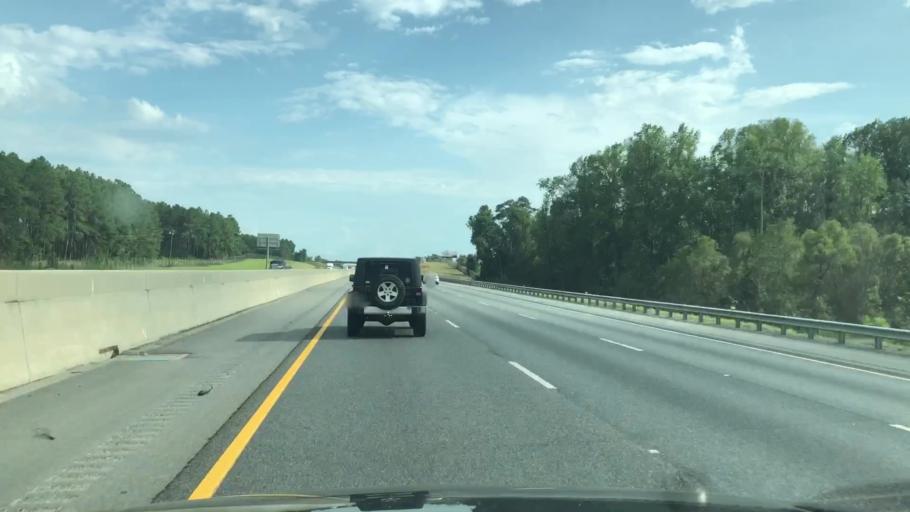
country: US
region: Georgia
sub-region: Tift County
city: Tifton
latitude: 31.5368
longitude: -83.5276
